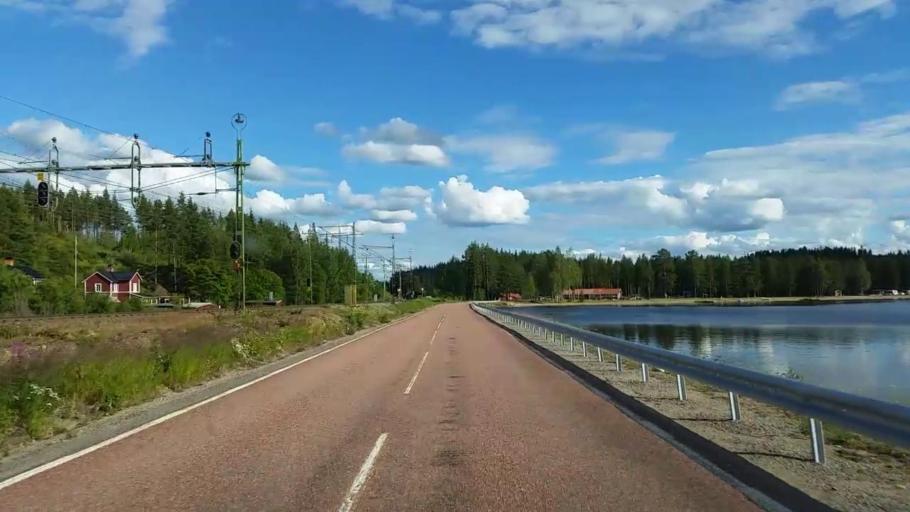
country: SE
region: Gaevleborg
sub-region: Ljusdals Kommun
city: Farila
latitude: 62.0199
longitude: 15.9036
